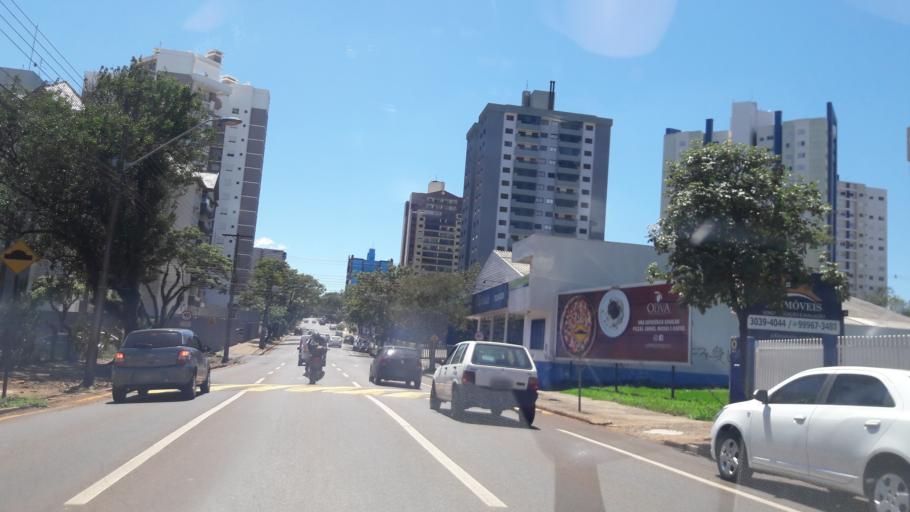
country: BR
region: Parana
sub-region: Cascavel
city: Cascavel
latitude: -24.9516
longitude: -53.4684
